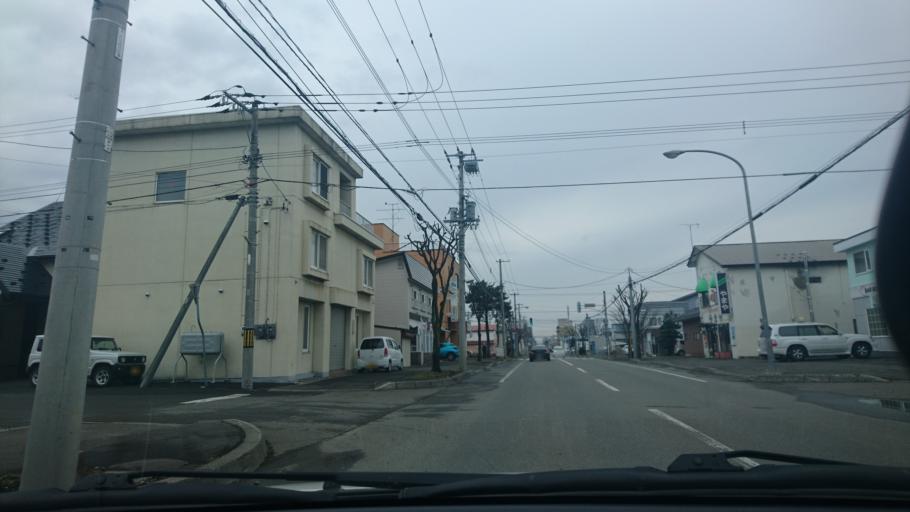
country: JP
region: Hokkaido
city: Obihiro
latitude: 42.9334
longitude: 143.1959
